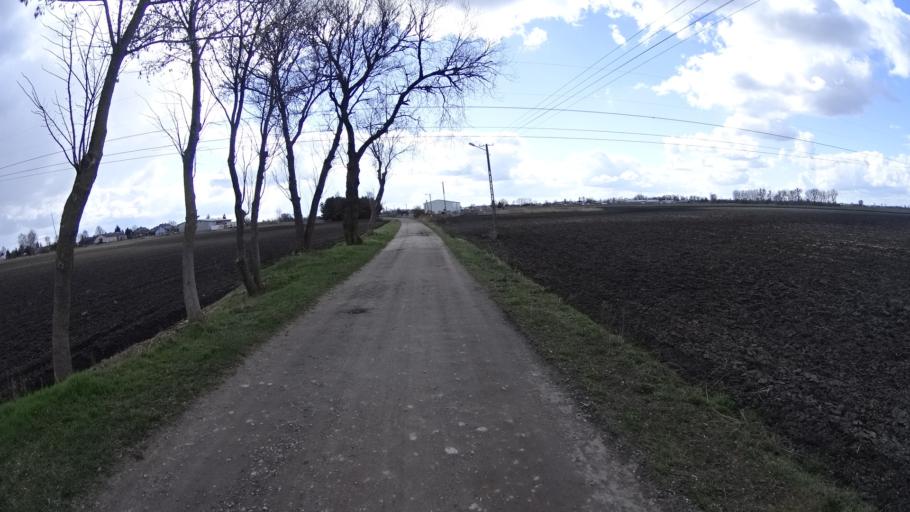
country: PL
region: Masovian Voivodeship
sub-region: Powiat warszawski zachodni
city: Jozefow
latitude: 52.2268
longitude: 20.7258
